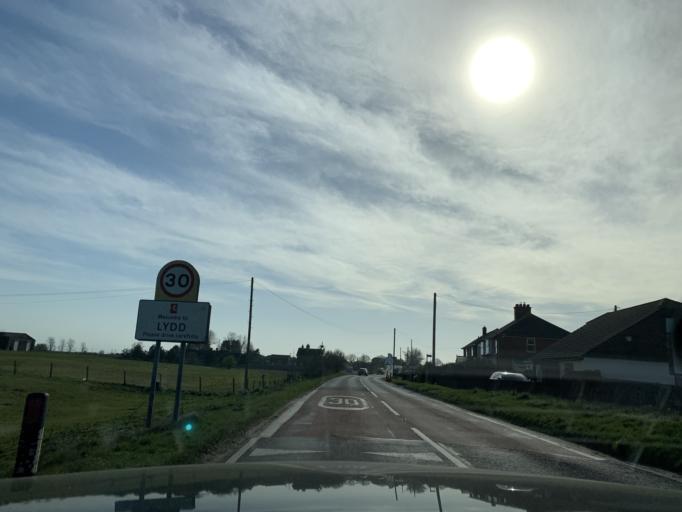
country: GB
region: England
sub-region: Kent
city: Lydd
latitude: 50.9590
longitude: 0.9182
